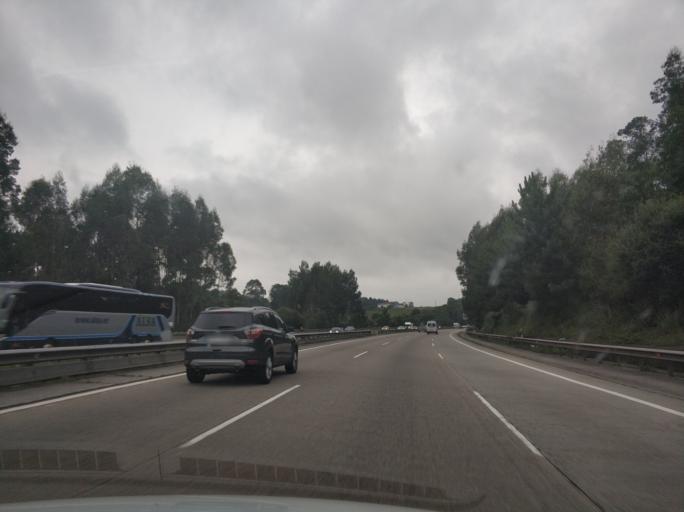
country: ES
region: Asturias
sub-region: Province of Asturias
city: Corvera de Asturias
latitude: 43.5039
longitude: -5.8020
